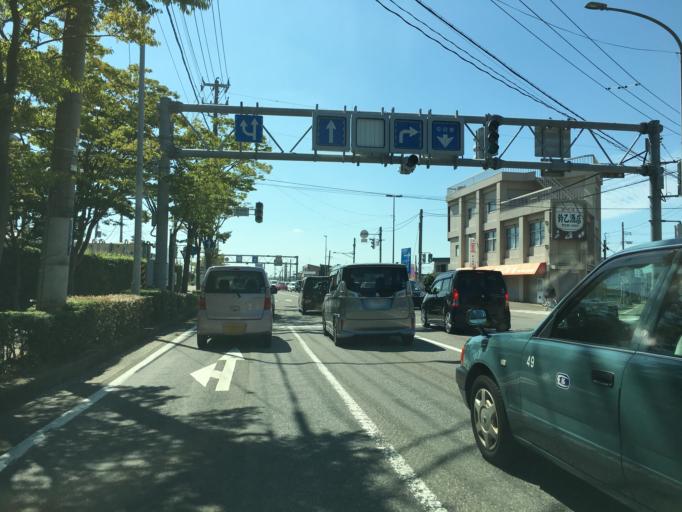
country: JP
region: Niigata
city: Niigata-shi
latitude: 37.9017
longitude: 139.0146
